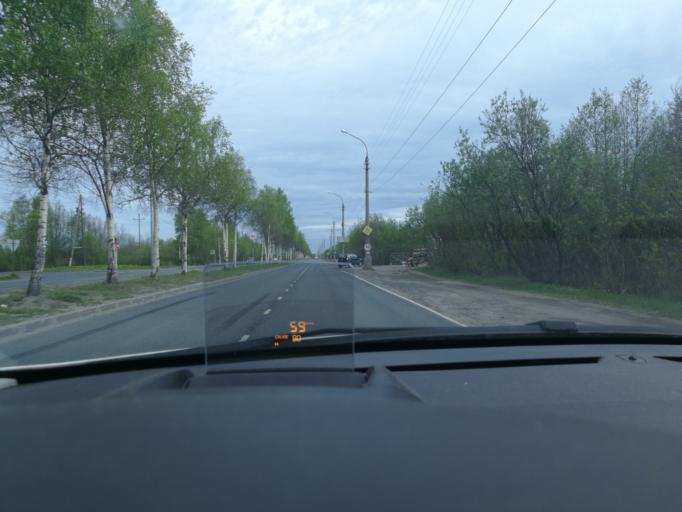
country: RU
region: Arkhangelskaya
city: Arkhangel'sk
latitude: 64.6156
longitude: 40.5256
